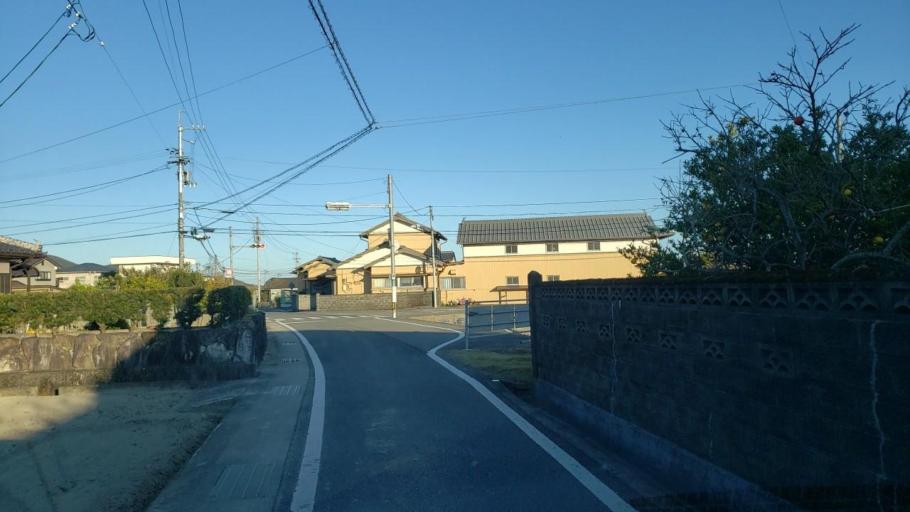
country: JP
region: Tokushima
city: Kamojimacho-jogejima
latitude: 34.0910
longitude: 134.2645
